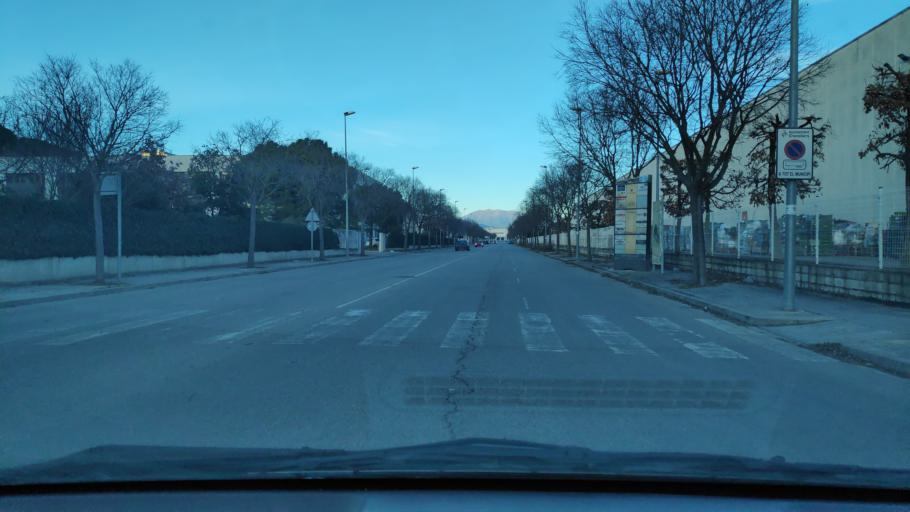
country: ES
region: Catalonia
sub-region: Provincia de Barcelona
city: Montmelo
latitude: 41.5667
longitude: 2.2641
